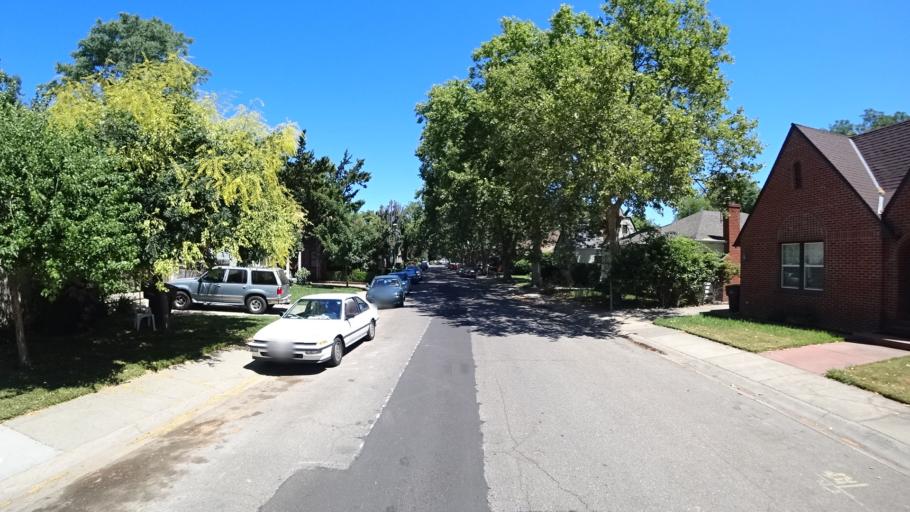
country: US
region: California
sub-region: Sacramento County
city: Sacramento
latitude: 38.5513
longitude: -121.4596
